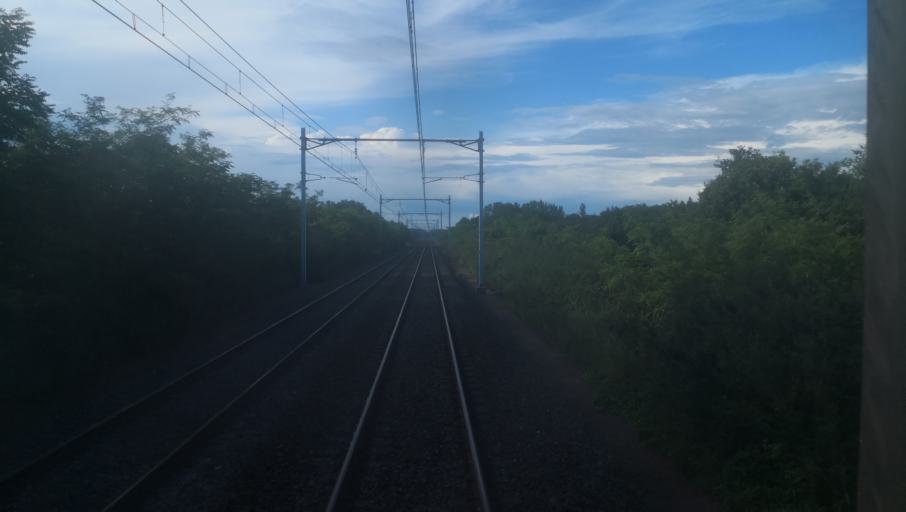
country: FR
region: Centre
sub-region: Departement du Loir-et-Cher
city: Theillay
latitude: 47.3246
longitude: 2.0452
